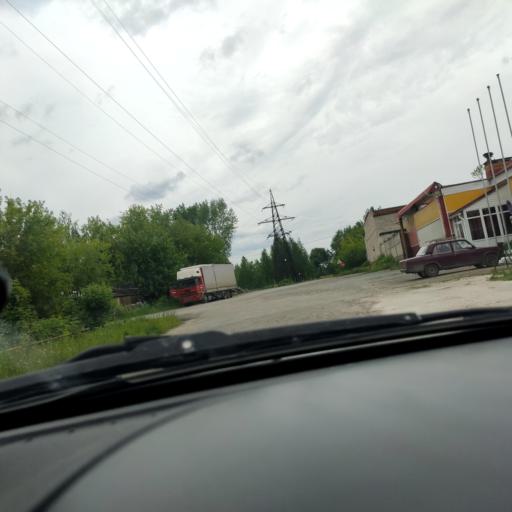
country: RU
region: Perm
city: Overyata
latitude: 58.0636
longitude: 55.8224
